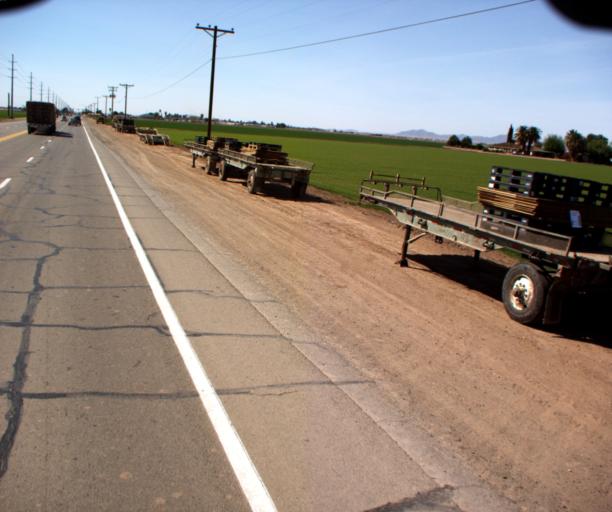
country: US
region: Arizona
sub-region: Yuma County
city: Fortuna Foothills
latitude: 32.6993
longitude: -114.5152
